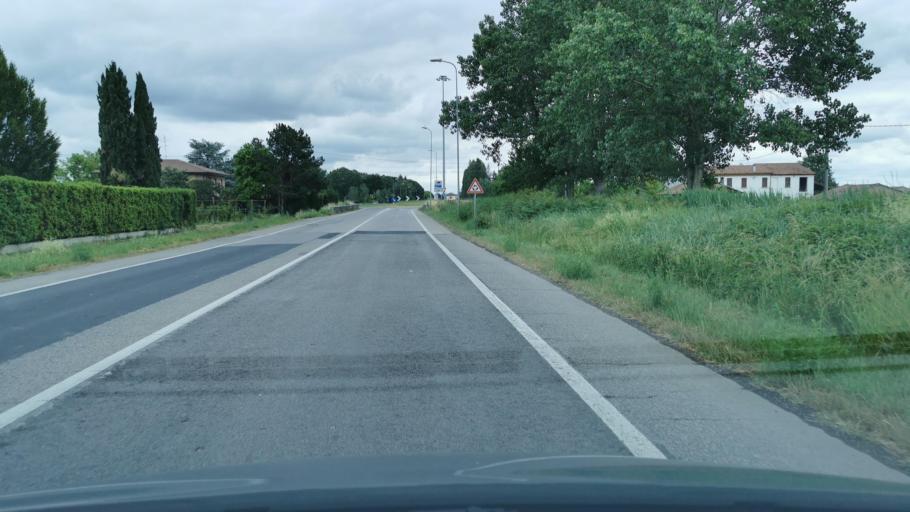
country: IT
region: Emilia-Romagna
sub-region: Provincia di Ravenna
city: Bagnacavallo
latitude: 44.4039
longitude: 11.9650
